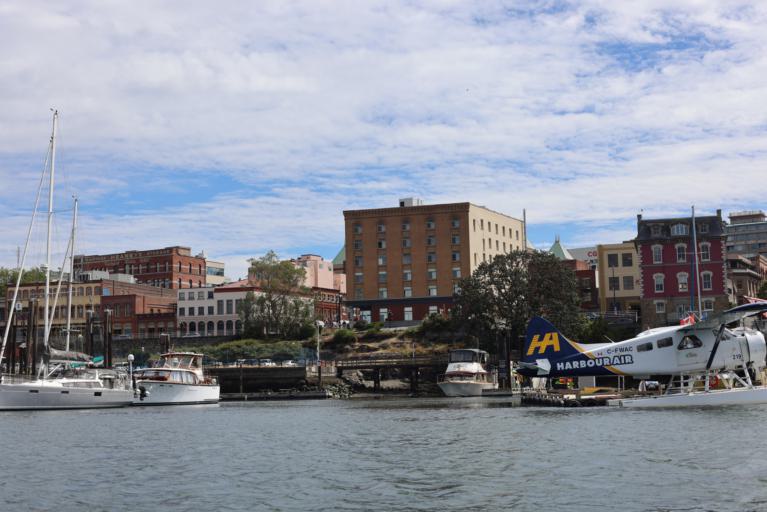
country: CA
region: British Columbia
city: Victoria
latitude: 48.4243
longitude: -123.3724
